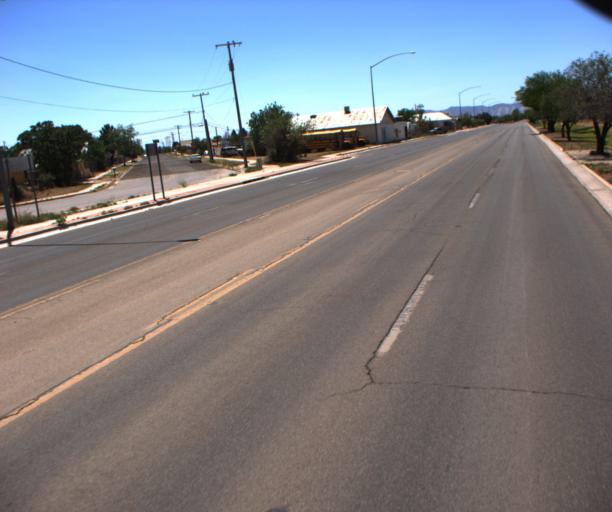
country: US
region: Arizona
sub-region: Cochise County
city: Douglas
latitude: 31.3560
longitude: -109.5499
